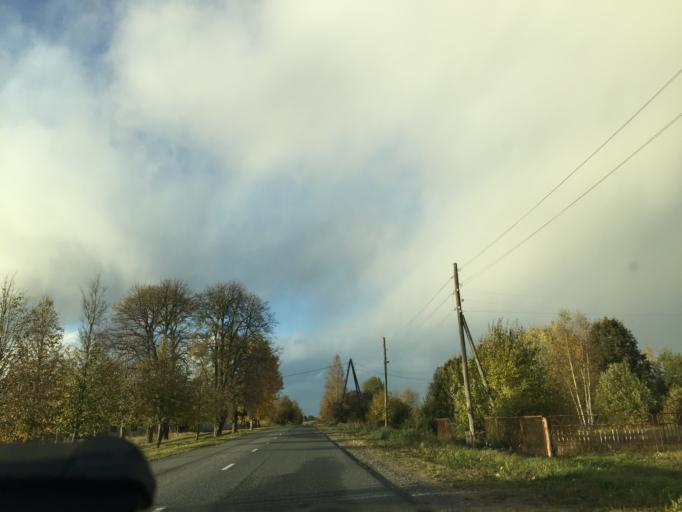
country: LV
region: Broceni
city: Broceni
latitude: 56.8584
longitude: 22.3829
